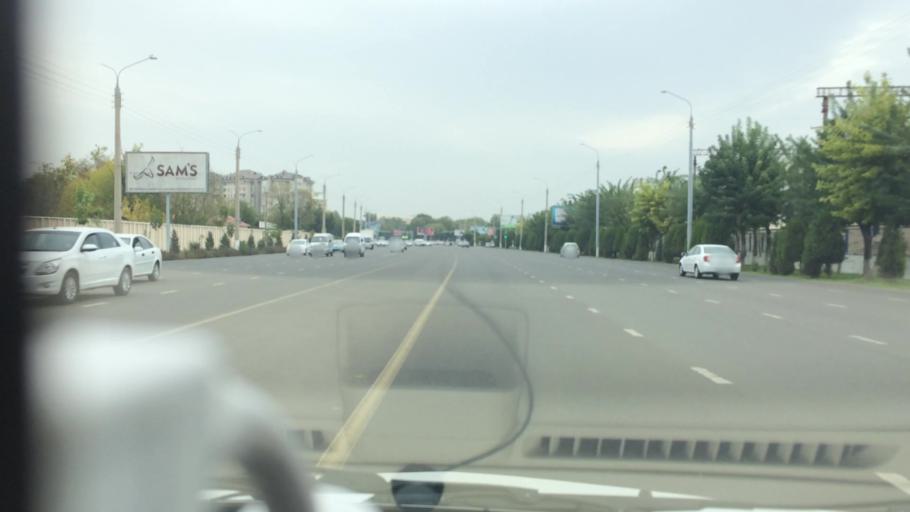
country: UZ
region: Toshkent Shahri
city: Tashkent
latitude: 41.2859
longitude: 69.2798
